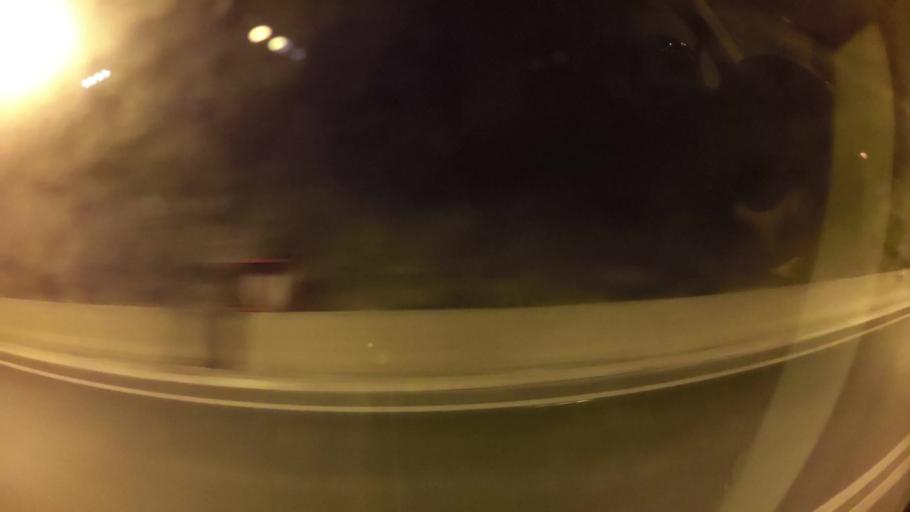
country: CL
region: Santiago Metropolitan
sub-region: Provincia de Chacabuco
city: Chicureo Abajo
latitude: -33.3412
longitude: -70.6257
